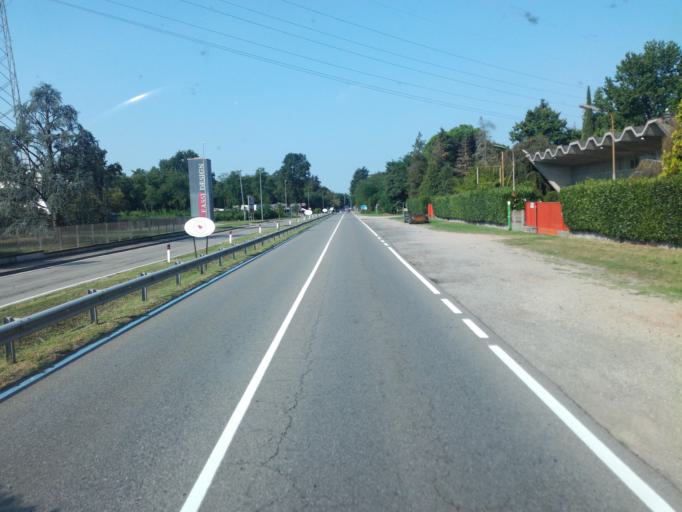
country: IT
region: Lombardy
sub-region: Provincia di Varese
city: Cascina Elisa
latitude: 45.5968
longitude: 8.7911
